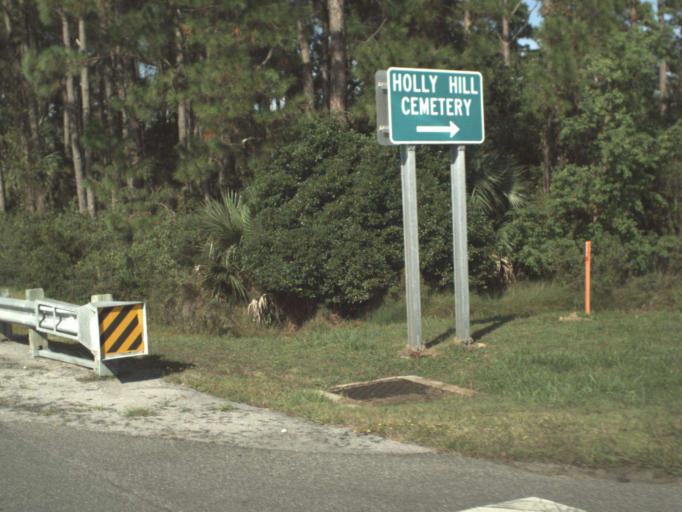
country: US
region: Florida
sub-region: Gulf County
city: Port Saint Joe
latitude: 29.7902
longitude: -85.3018
